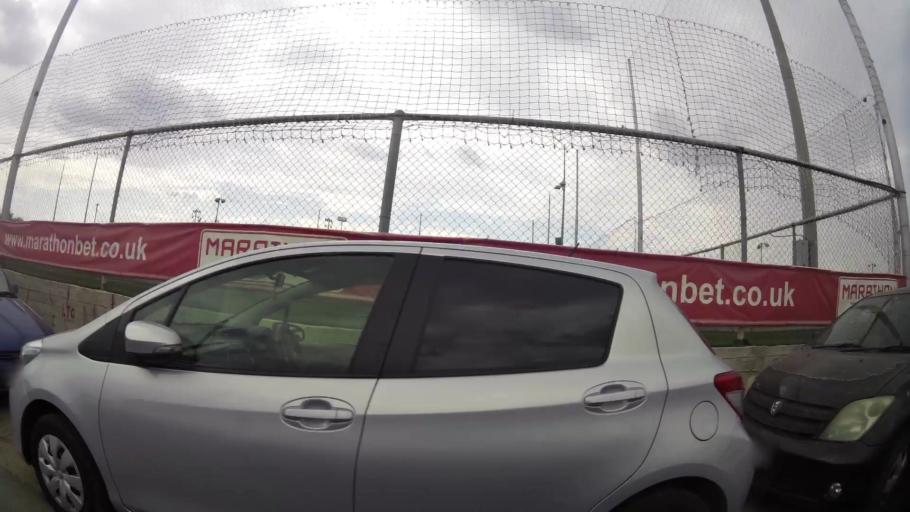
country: CY
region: Lefkosia
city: Geri
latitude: 35.1169
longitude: 33.3657
